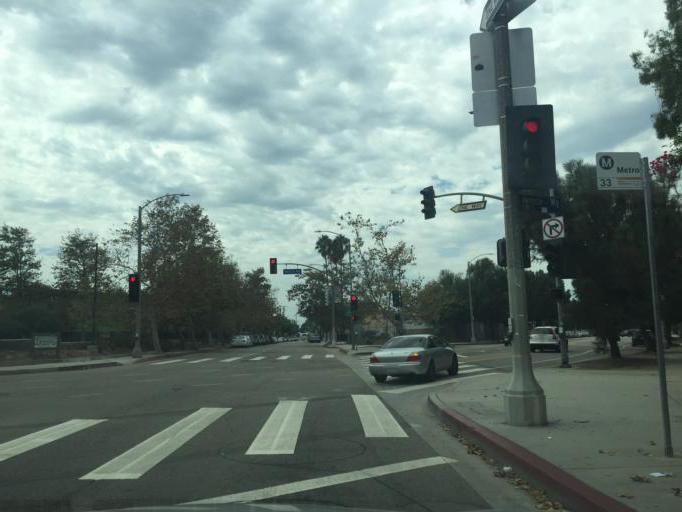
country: US
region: California
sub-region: Los Angeles County
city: Marina del Rey
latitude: 33.9877
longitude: -118.4658
